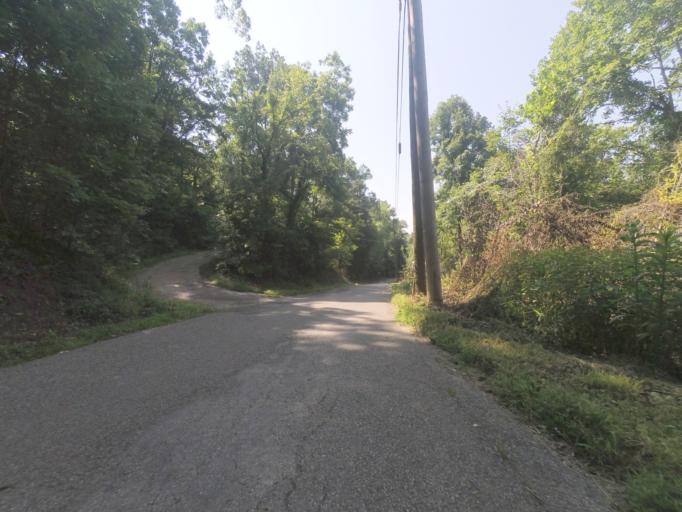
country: US
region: West Virginia
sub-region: Cabell County
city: Huntington
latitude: 38.4323
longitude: -82.4486
